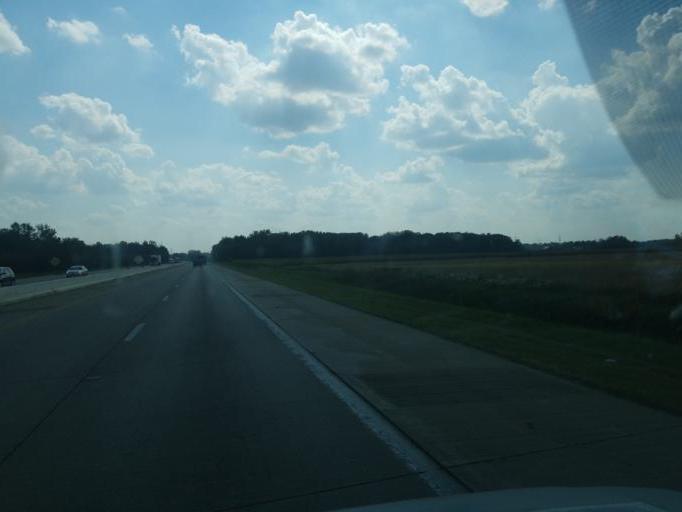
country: US
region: Indiana
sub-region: Allen County
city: New Haven
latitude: 41.1054
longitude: -84.9959
